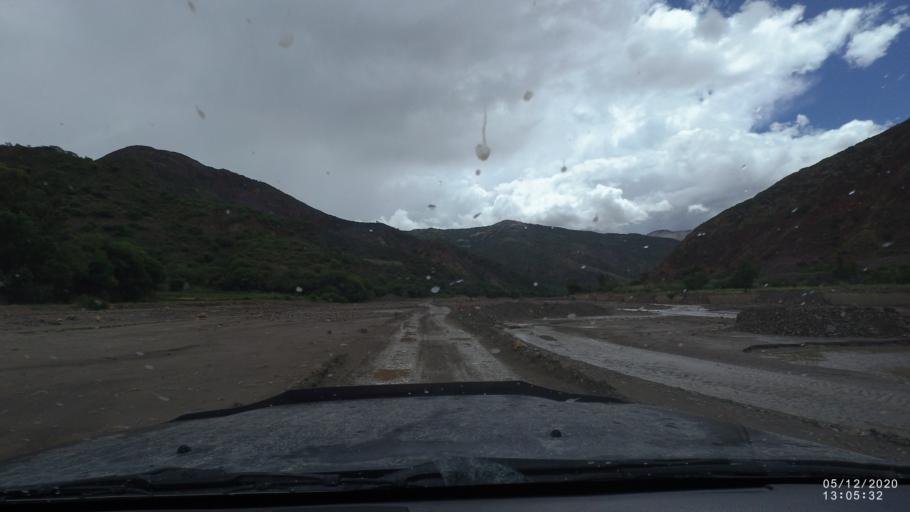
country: BO
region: Cochabamba
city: Sipe Sipe
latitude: -17.5549
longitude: -66.4424
